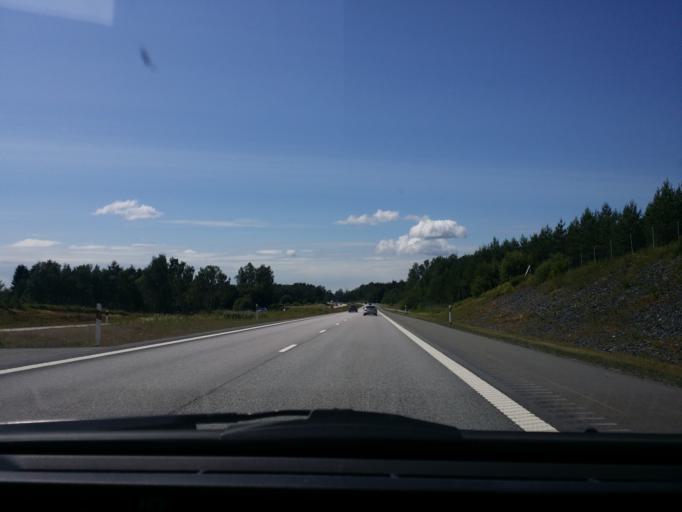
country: SE
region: OErebro
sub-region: Lindesbergs Kommun
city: Fellingsbro
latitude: 59.3258
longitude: 15.4950
